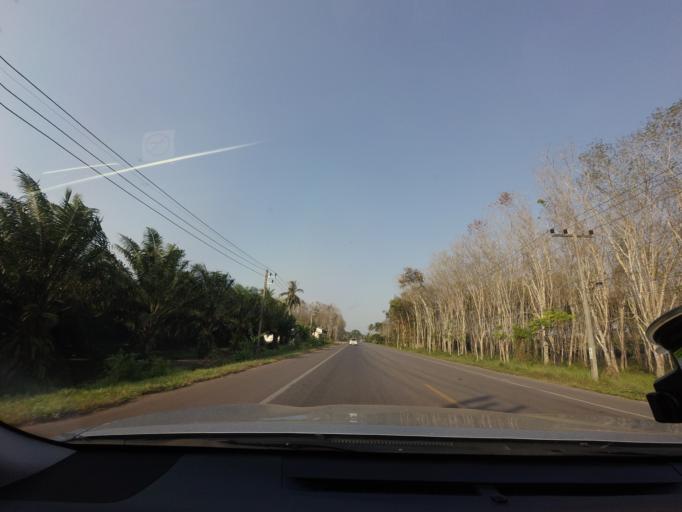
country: TH
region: Surat Thani
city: Phrasaeng
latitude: 8.5774
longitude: 99.2772
